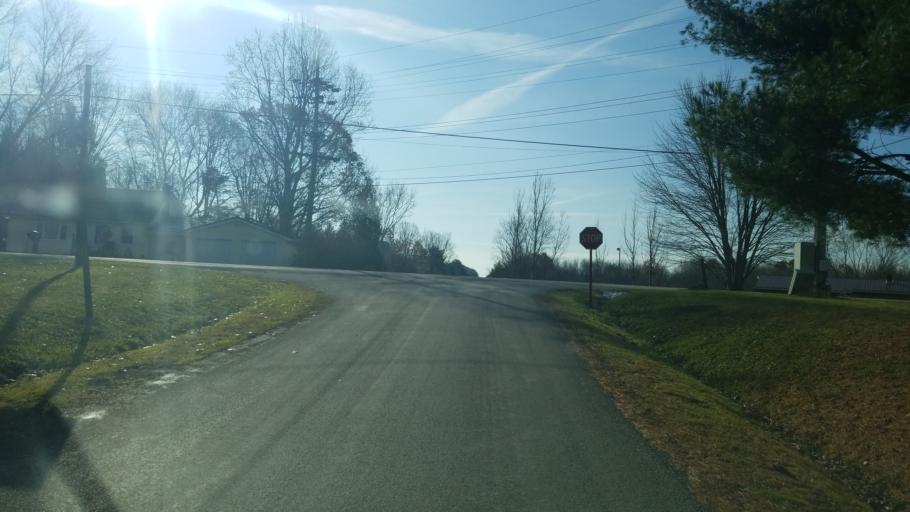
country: US
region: Ohio
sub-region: Ashtabula County
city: North Kingsville
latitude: 41.8412
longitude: -80.6841
